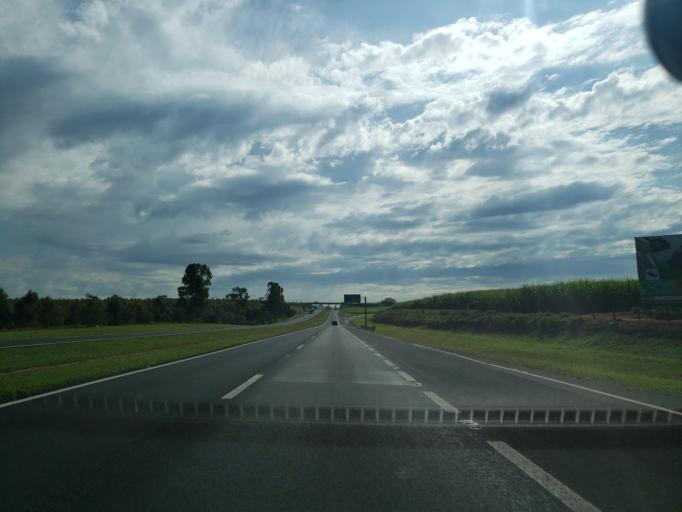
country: BR
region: Sao Paulo
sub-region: Cafelandia
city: Cafelandia
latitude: -21.8798
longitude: -49.5551
